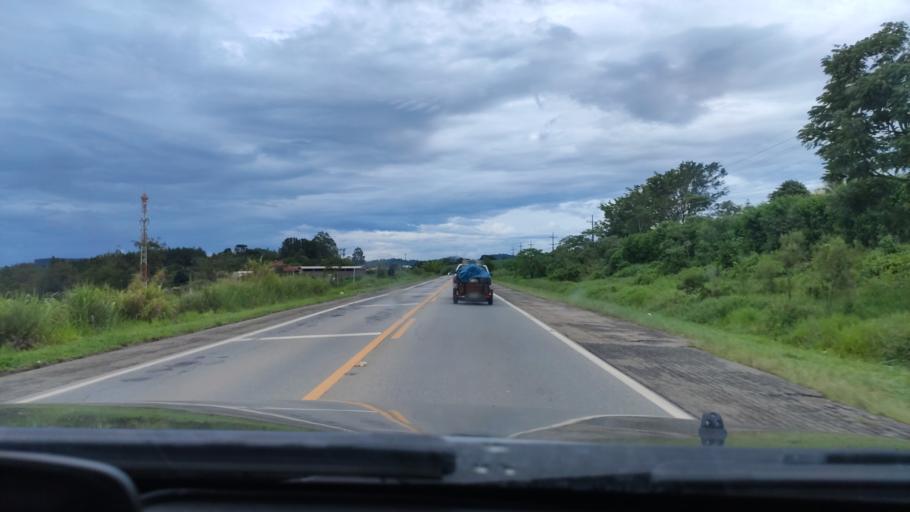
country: BR
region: Sao Paulo
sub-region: Braganca Paulista
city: Braganca Paulista
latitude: -22.8647
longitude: -46.5370
